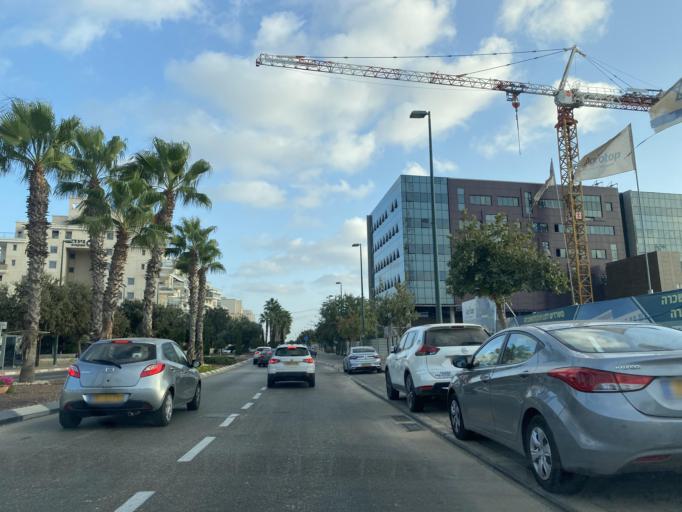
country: IL
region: Central District
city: Netanya
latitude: 32.3112
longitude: 34.8699
